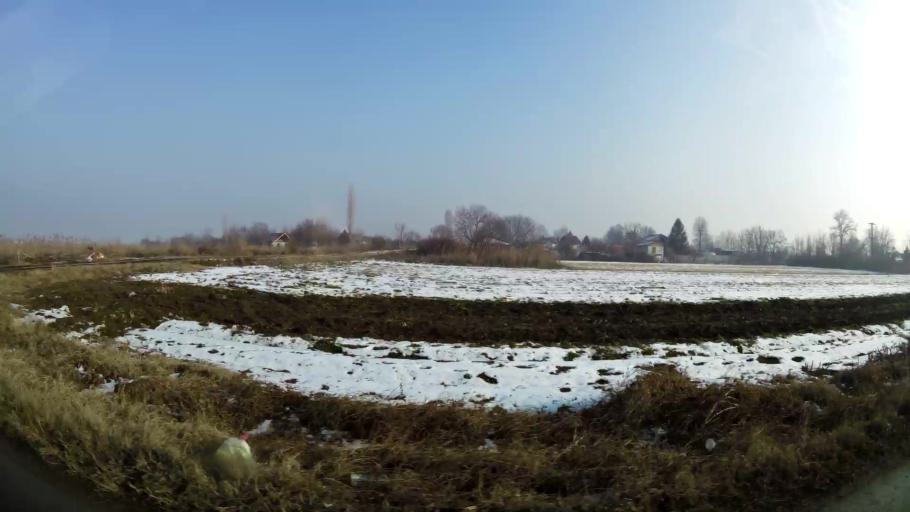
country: MK
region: Petrovec
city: Petrovec
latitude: 41.9473
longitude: 21.5962
